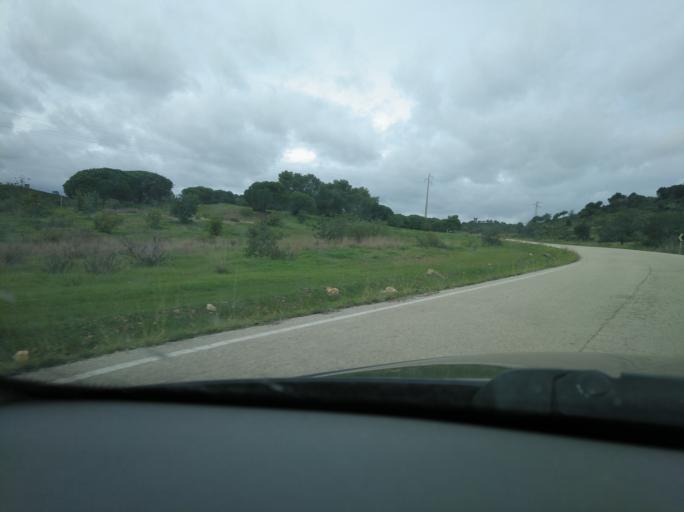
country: PT
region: Faro
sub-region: Vila Real de Santo Antonio
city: Monte Gordo
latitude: 37.2059
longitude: -7.4864
